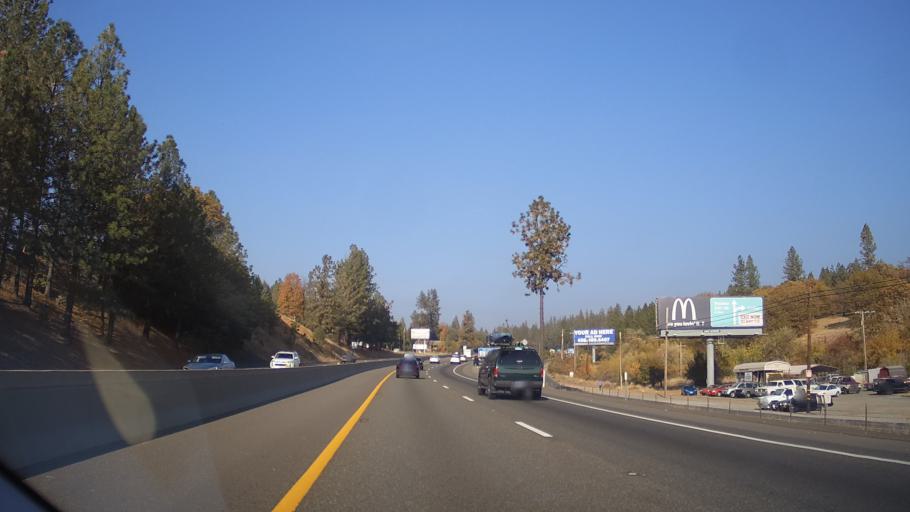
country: US
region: California
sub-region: Placer County
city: Colfax
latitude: 39.0856
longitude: -120.9561
